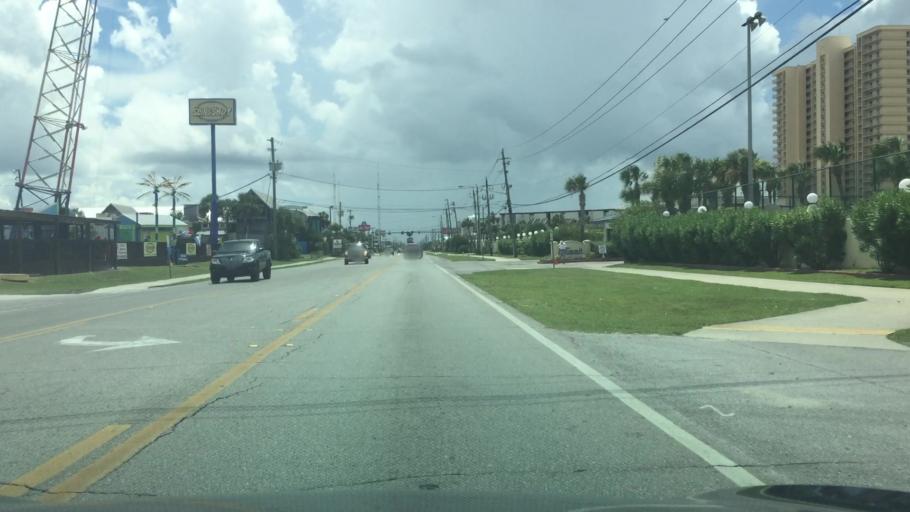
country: US
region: Florida
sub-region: Bay County
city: Panama City Beach
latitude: 30.1697
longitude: -85.7923
